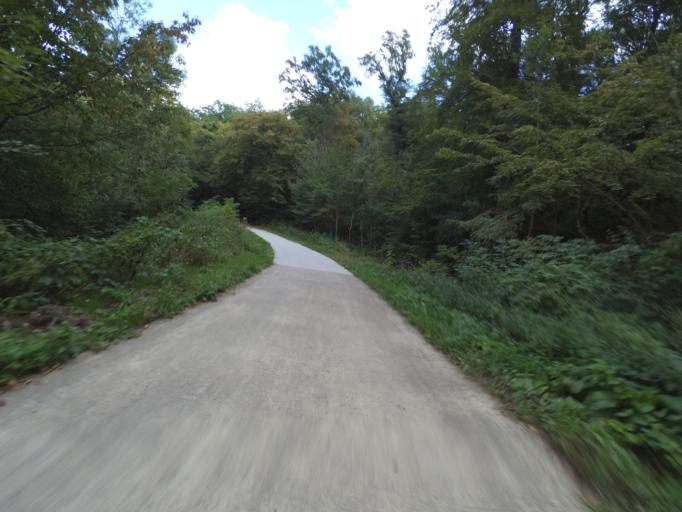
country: LU
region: Grevenmacher
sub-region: Canton de Remich
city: Bous
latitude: 49.5321
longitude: 6.3325
